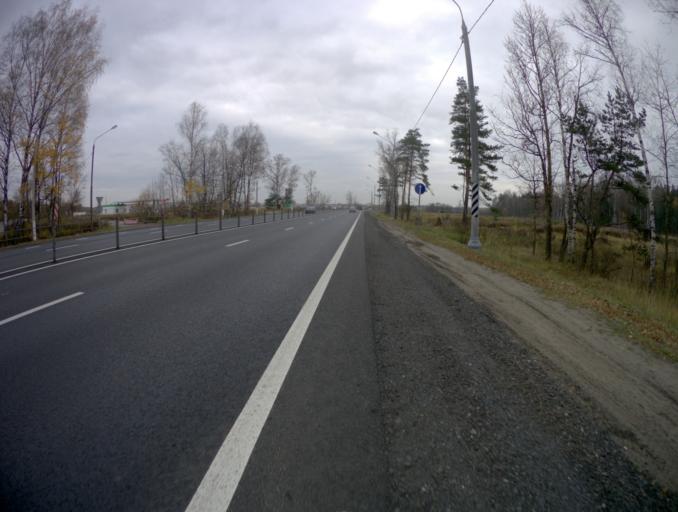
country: RU
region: Moskovskaya
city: Malaya Dubna
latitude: 55.8700
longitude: 38.9638
